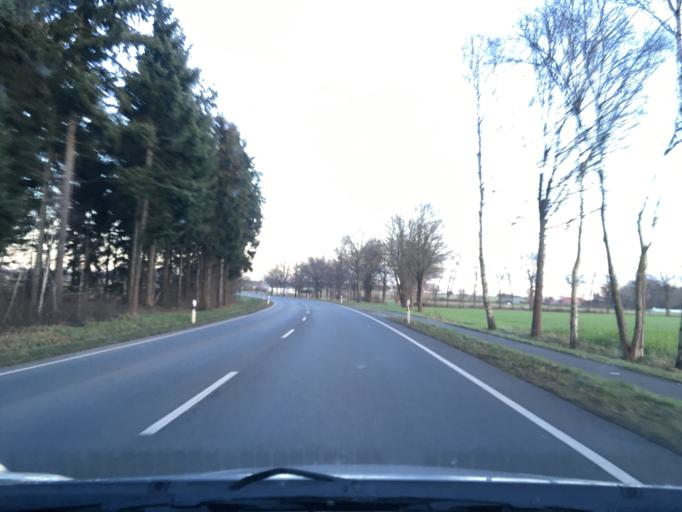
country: DE
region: Lower Saxony
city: Uelzen
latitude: 52.9733
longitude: 10.6117
